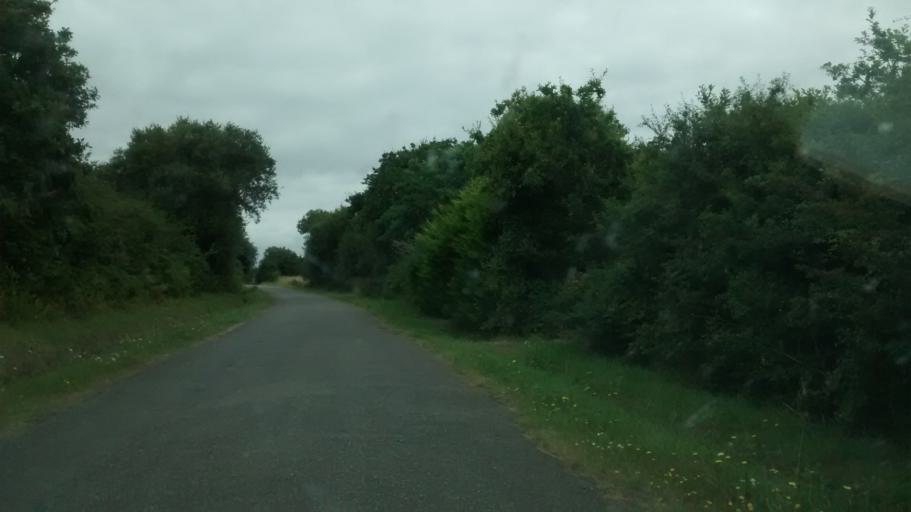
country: FR
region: Brittany
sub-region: Departement du Finistere
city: Lanveoc
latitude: 48.3318
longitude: -4.4361
